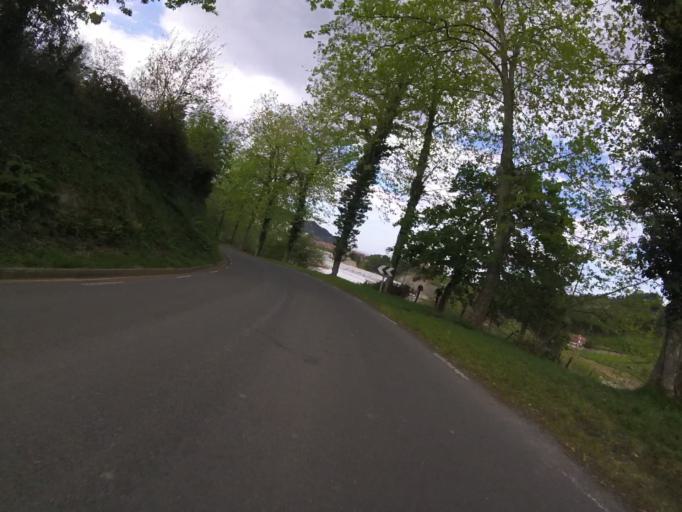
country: ES
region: Basque Country
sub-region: Provincia de Guipuzcoa
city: Zarautz
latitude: 43.2711
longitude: -2.1665
